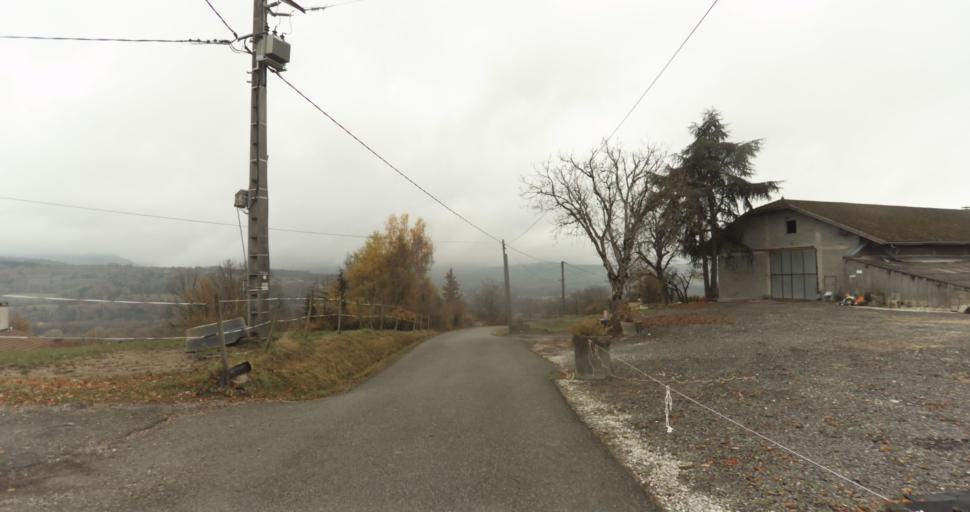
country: FR
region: Rhone-Alpes
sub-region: Departement de la Haute-Savoie
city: Groisy
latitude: 46.0221
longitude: 6.1976
